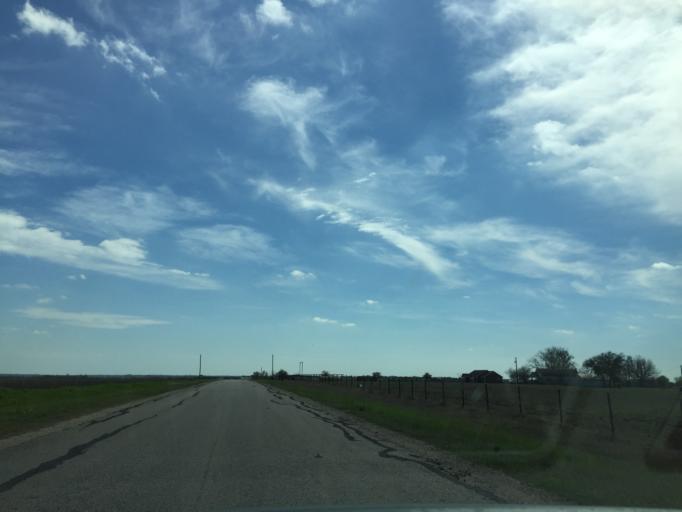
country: US
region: Texas
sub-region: Milam County
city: Thorndale
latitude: 30.5505
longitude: -97.2972
